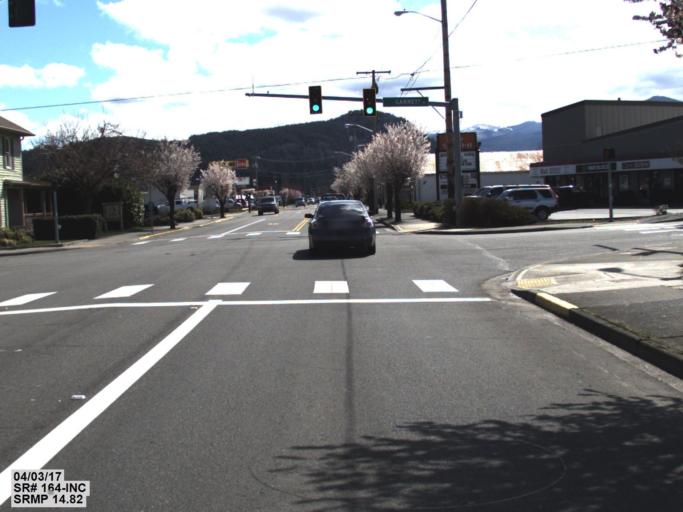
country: US
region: Washington
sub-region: King County
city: Enumclaw
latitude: 47.2020
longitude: -121.9864
